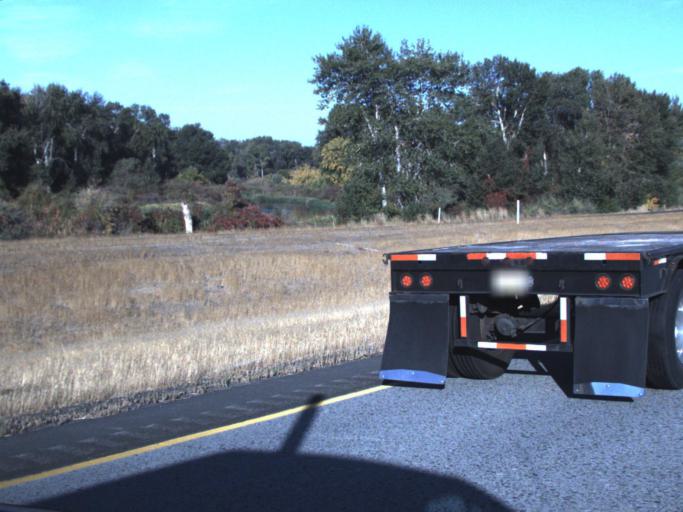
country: US
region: Washington
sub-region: Yakima County
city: Wapato
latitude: 46.4437
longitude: -120.3469
